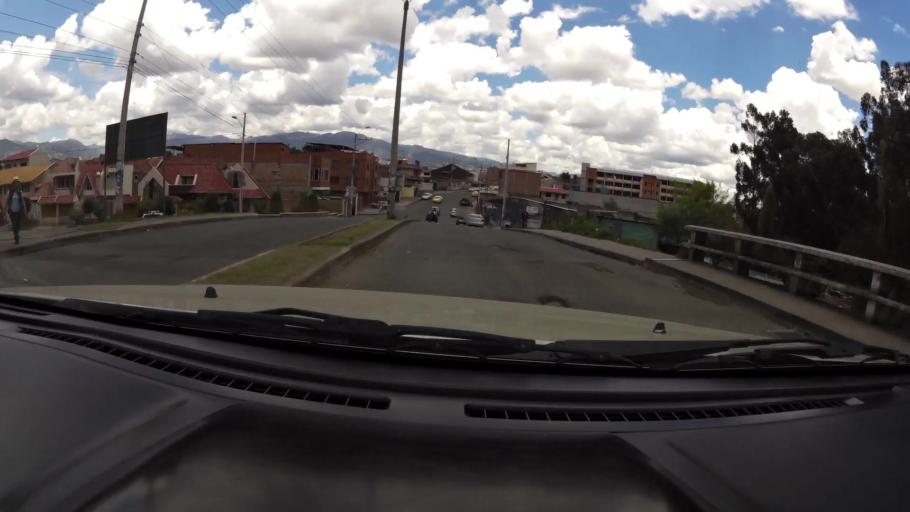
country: EC
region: Azuay
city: Cuenca
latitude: -2.9187
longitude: -79.0170
